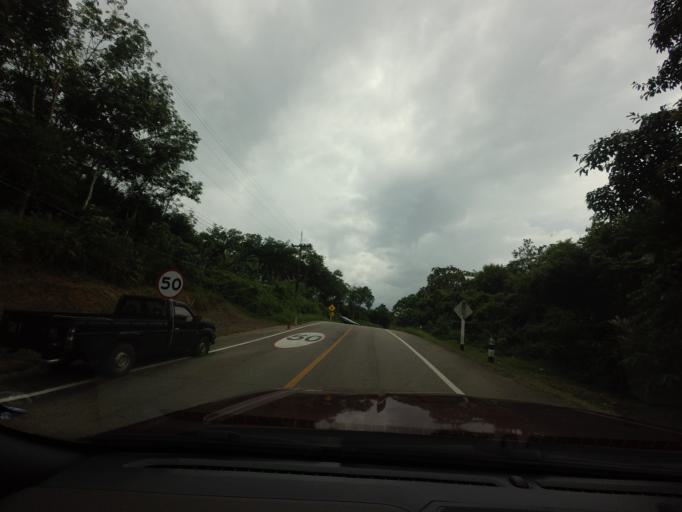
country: TH
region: Narathiwat
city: Sukhirin
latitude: 5.9780
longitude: 101.7060
